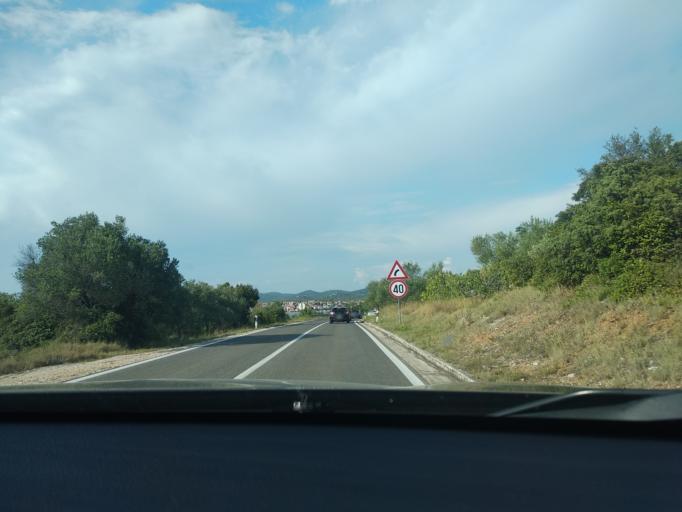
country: HR
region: Sibensko-Kniniska
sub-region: Grad Sibenik
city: Pirovac
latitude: 43.8004
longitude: 15.6748
